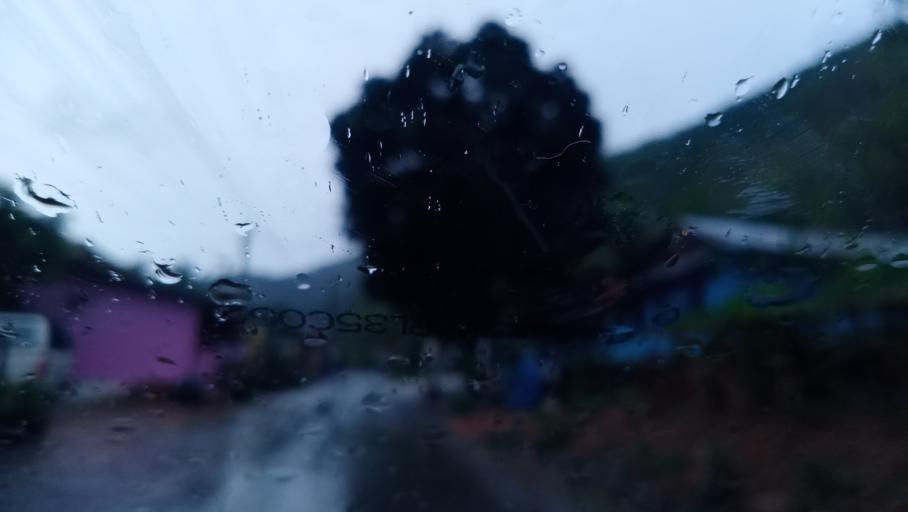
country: LA
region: Phongsali
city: Khoa
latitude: 21.0726
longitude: 102.5005
